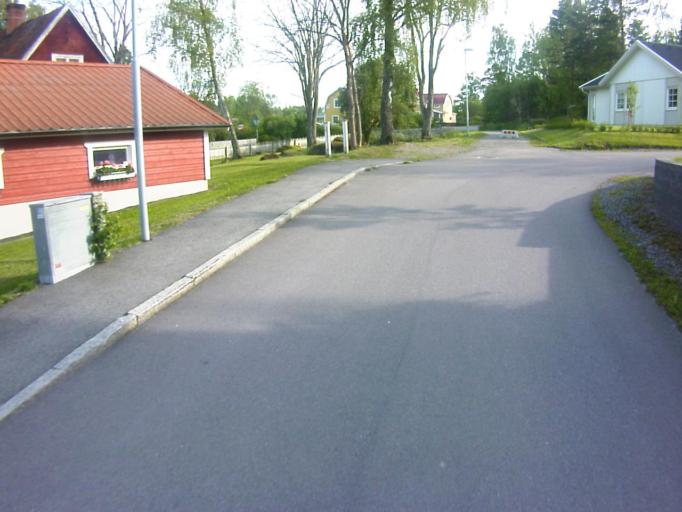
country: SE
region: Soedermanland
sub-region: Eskilstuna Kommun
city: Skogstorp
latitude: 59.3252
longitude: 16.4817
